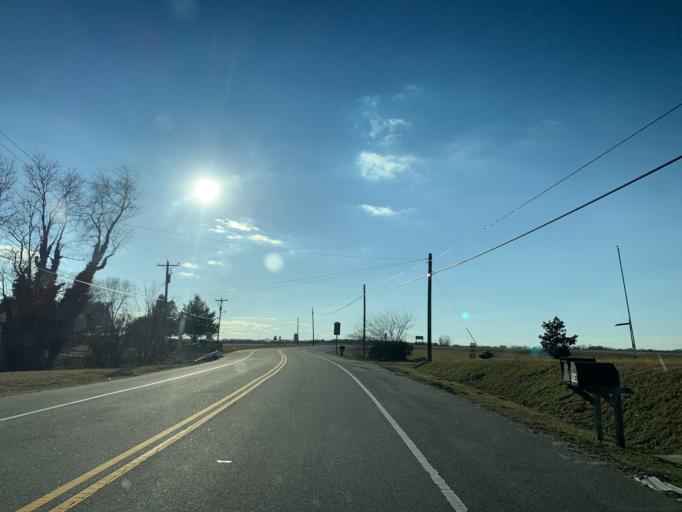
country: US
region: Maryland
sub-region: Queen Anne's County
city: Kingstown
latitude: 39.1386
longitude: -75.9908
